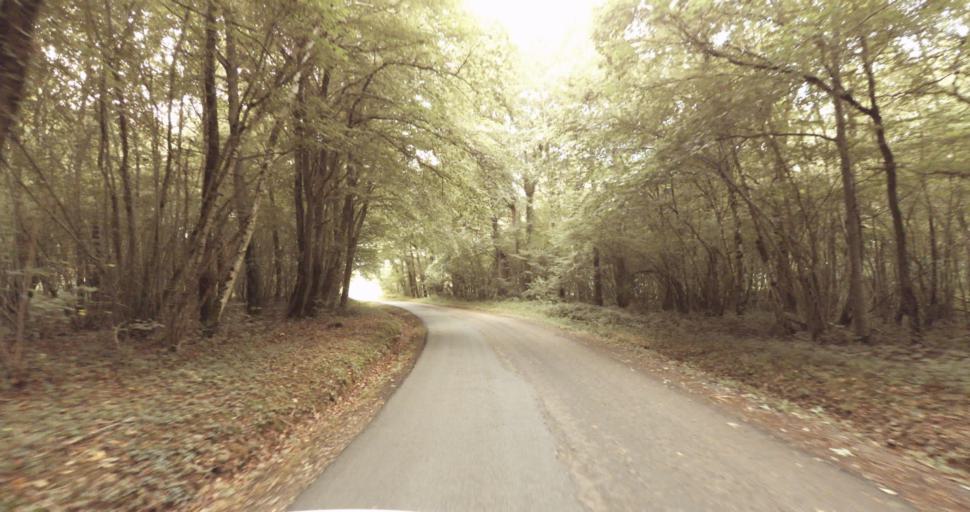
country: FR
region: Lower Normandy
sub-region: Departement de l'Orne
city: Trun
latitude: 48.9031
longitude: 0.1061
